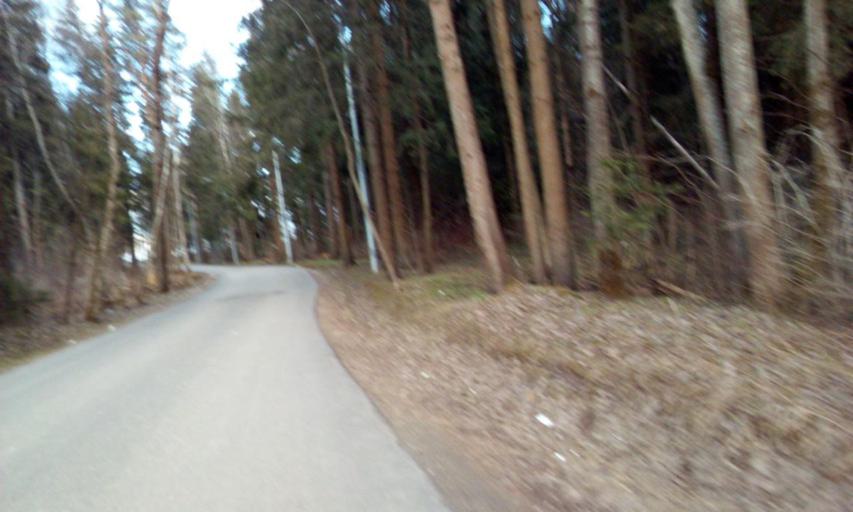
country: RU
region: Moskovskaya
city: Annino
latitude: 55.5551
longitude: 37.2302
